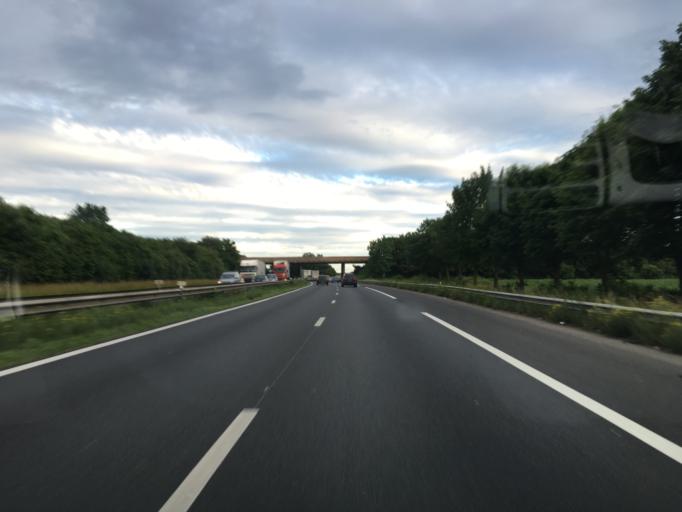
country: FR
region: Ile-de-France
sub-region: Departement de Seine-et-Marne
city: Brie-Comte-Robert
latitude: 48.6862
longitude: 2.5974
